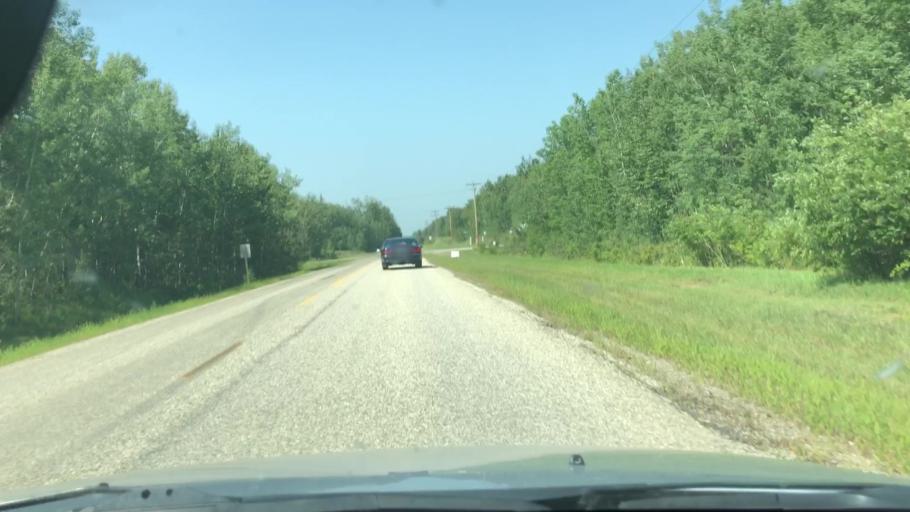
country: CA
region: Alberta
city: Devon
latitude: 53.4252
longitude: -113.7855
